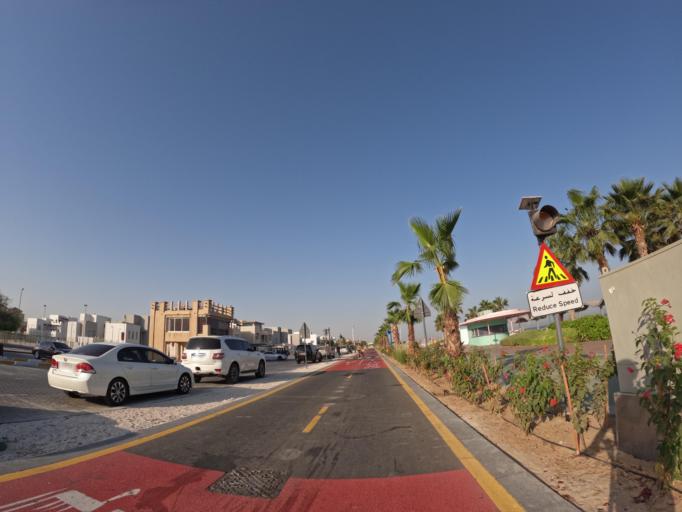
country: AE
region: Dubai
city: Dubai
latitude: 25.1792
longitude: 55.2205
